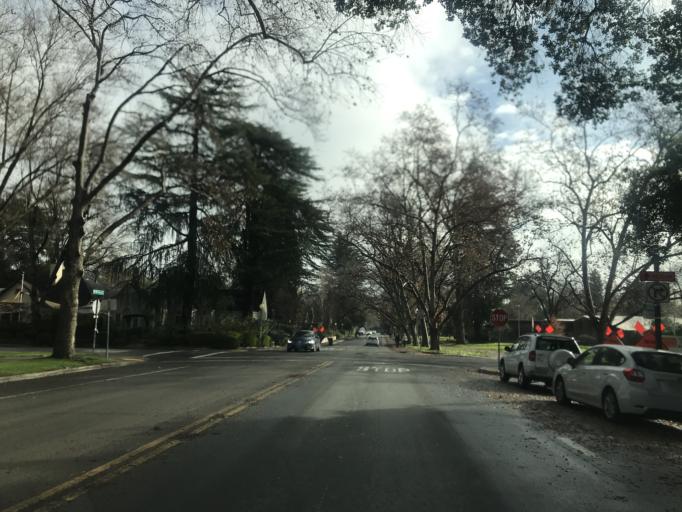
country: US
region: California
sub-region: Sacramento County
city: Sacramento
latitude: 38.5774
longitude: -121.4598
